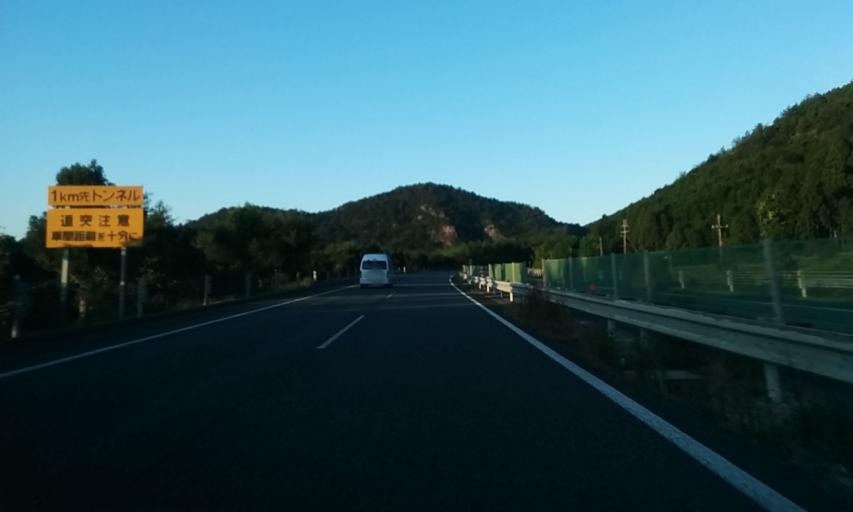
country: JP
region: Kyoto
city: Fukuchiyama
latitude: 35.1791
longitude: 135.1351
